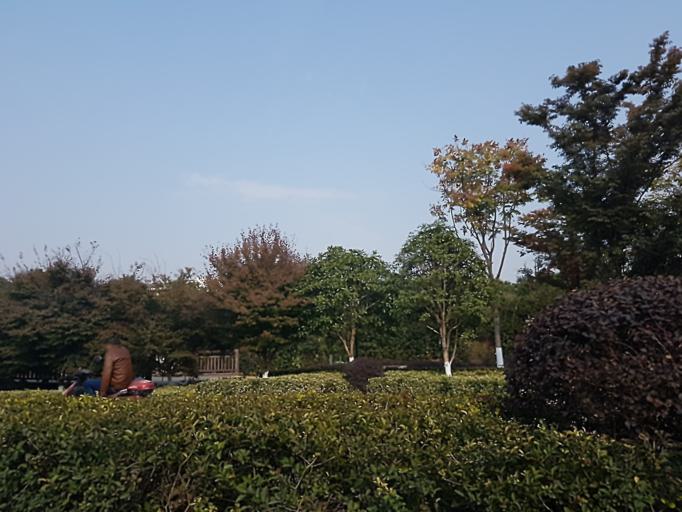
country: CN
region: Zhejiang Sheng
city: Cangqian
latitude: 30.2838
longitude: 120.0201
